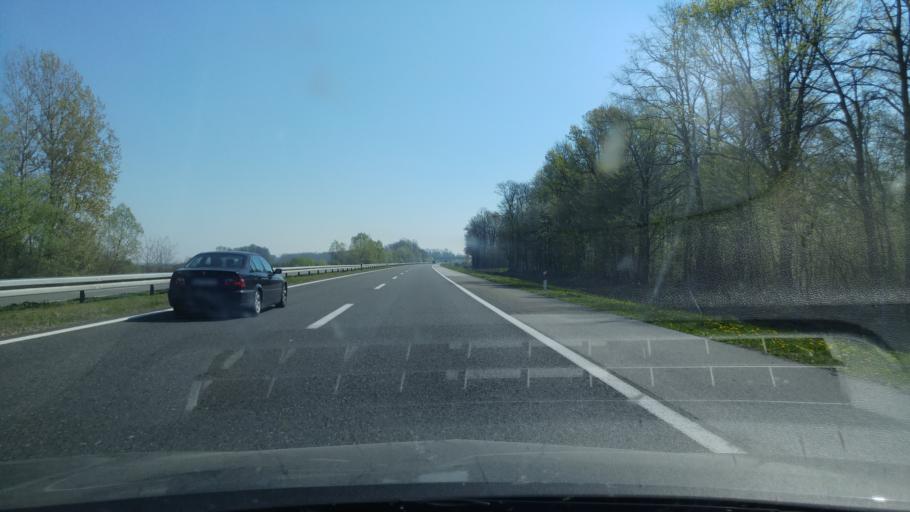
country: HR
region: Brodsko-Posavska
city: Garcin
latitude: 45.1555
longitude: 18.2290
